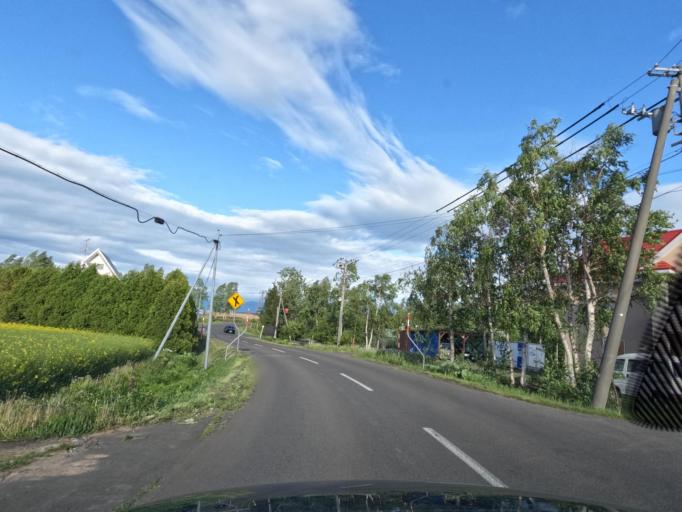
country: JP
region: Hokkaido
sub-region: Asahikawa-shi
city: Asahikawa
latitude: 43.6062
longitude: 142.4612
